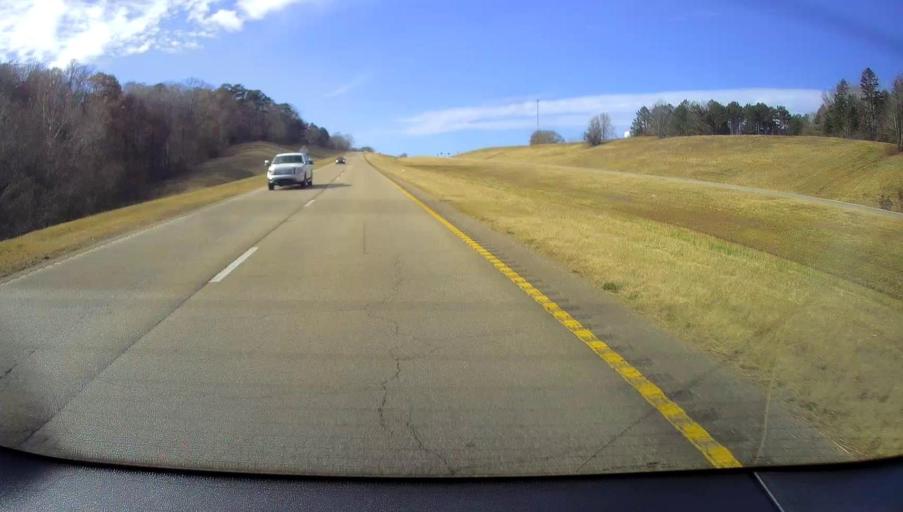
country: US
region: Mississippi
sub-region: Tippah County
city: Ripley
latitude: 34.9459
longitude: -88.7941
